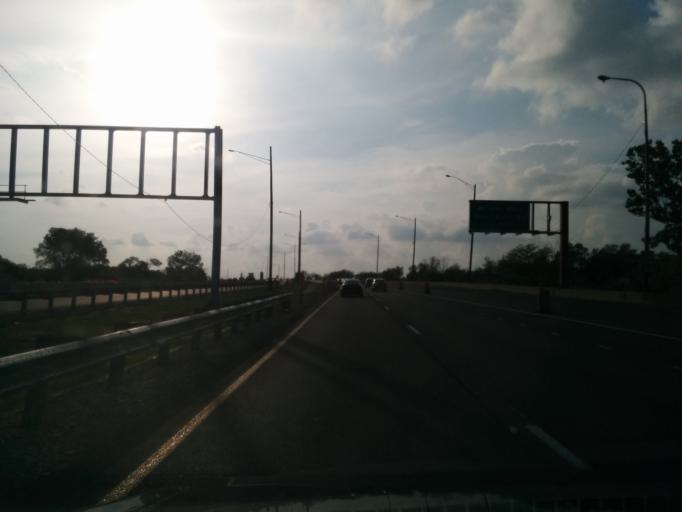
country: US
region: Illinois
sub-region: DuPage County
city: Roselle
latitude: 41.9962
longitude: -88.0849
